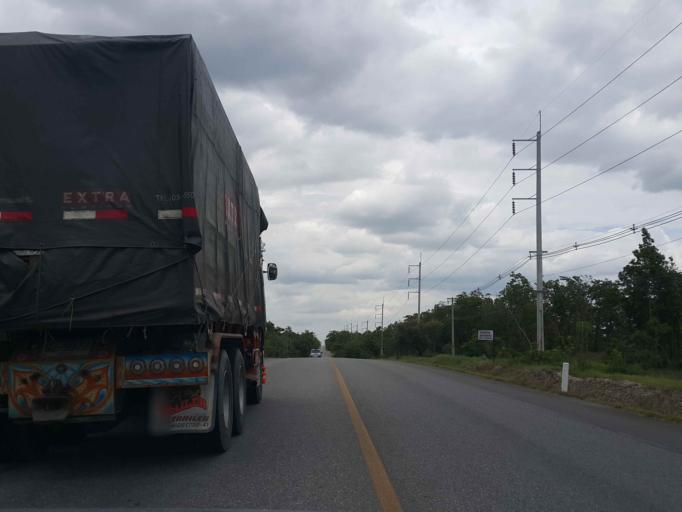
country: TH
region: Lamphun
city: Ban Hong
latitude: 18.4043
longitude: 98.8399
